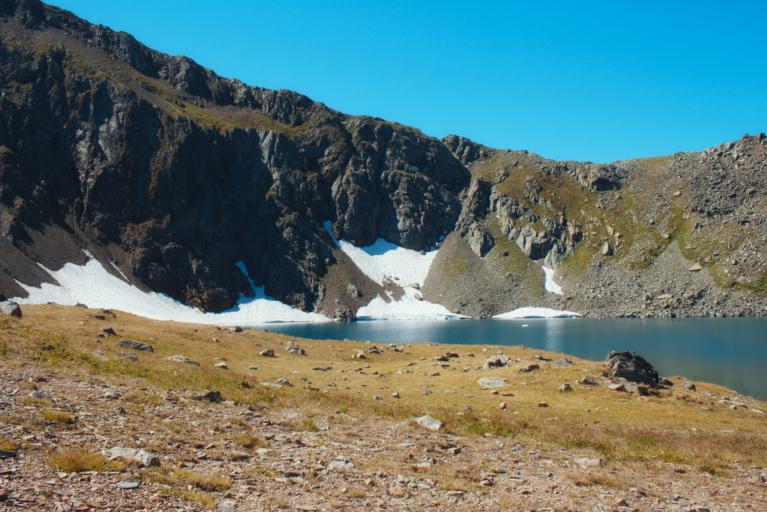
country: RU
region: Karachayevo-Cherkesiya
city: Mednogorskiy
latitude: 43.6158
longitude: 41.1122
